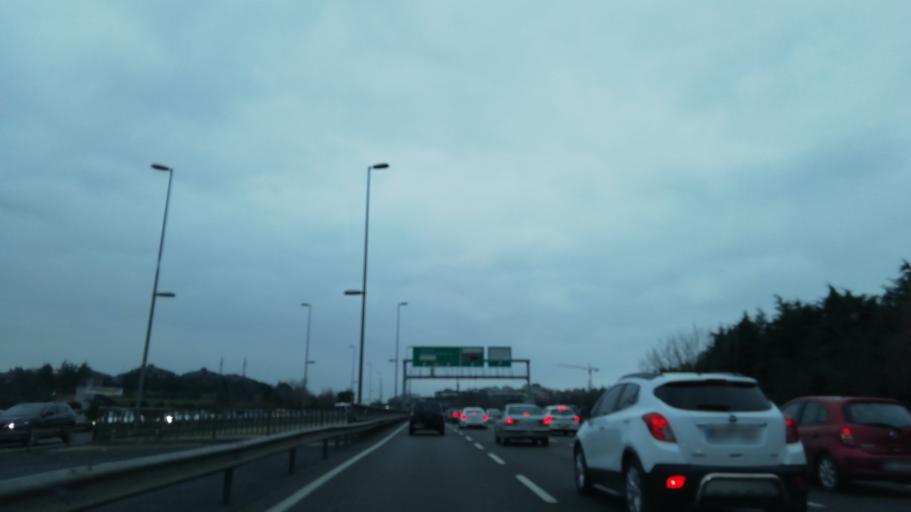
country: TR
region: Istanbul
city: UEskuedar
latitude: 41.0302
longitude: 29.0456
